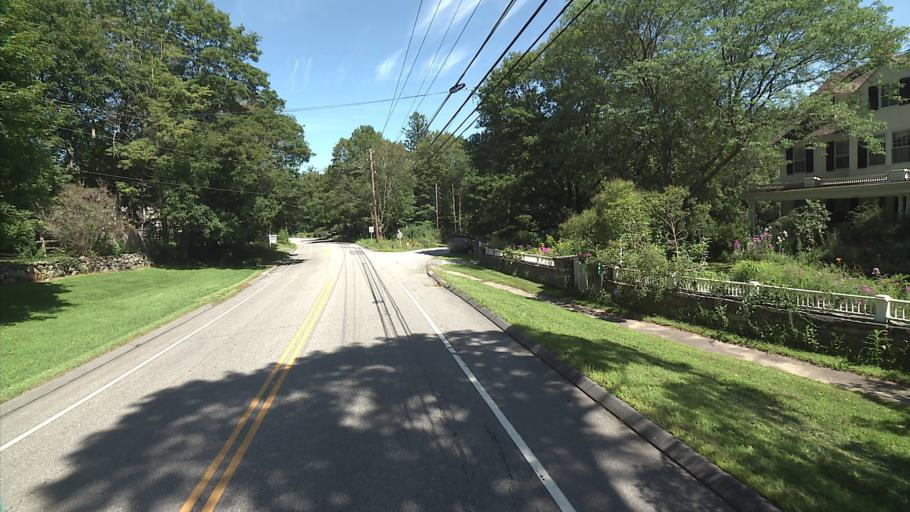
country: US
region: Connecticut
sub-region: Windham County
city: Windham
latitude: 41.7862
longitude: -72.0552
